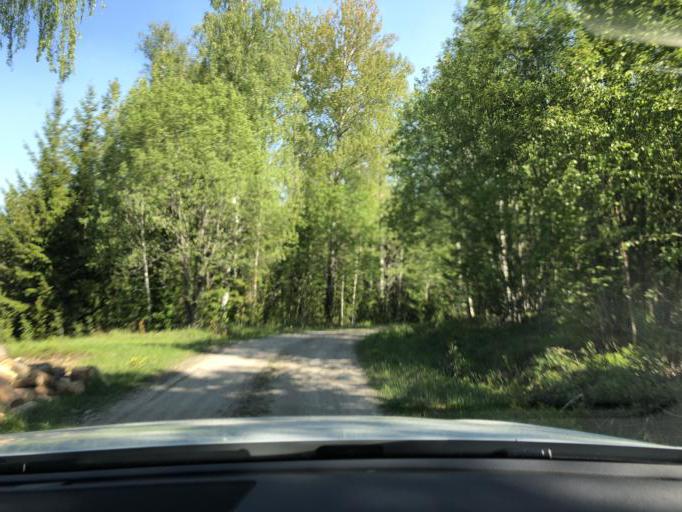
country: SE
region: Dalarna
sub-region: Avesta Kommun
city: Horndal
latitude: 60.2096
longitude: 16.4915
